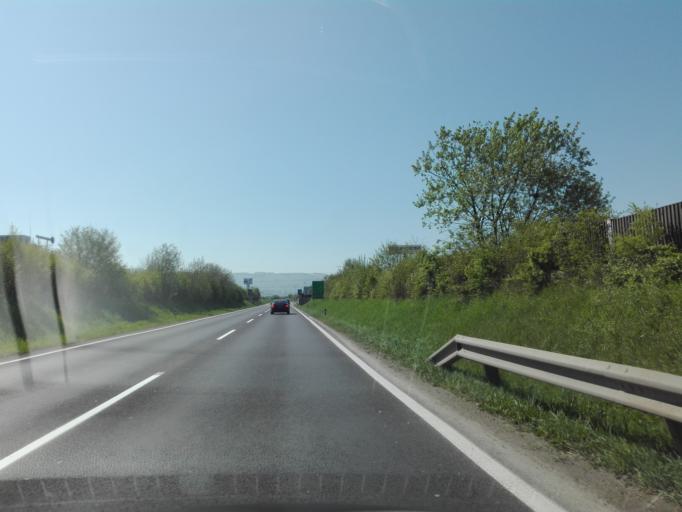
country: AT
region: Lower Austria
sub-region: Politischer Bezirk Amstetten
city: Haidershofen
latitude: 48.0741
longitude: 14.4280
